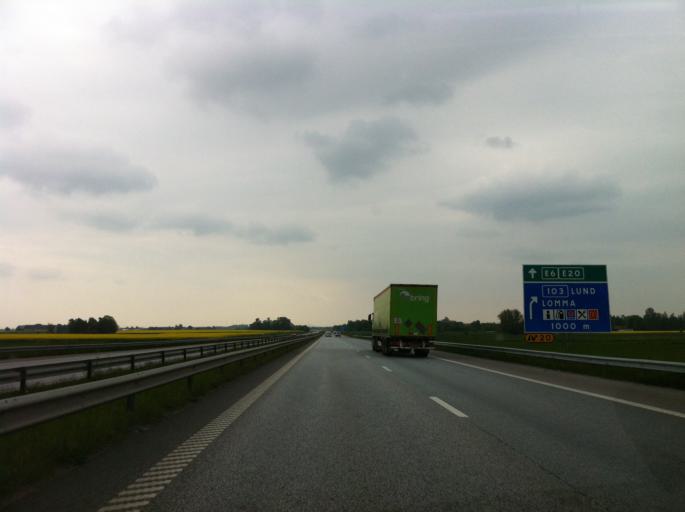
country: SE
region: Skane
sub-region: Lomma Kommun
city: Lomma
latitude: 55.6998
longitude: 13.0974
